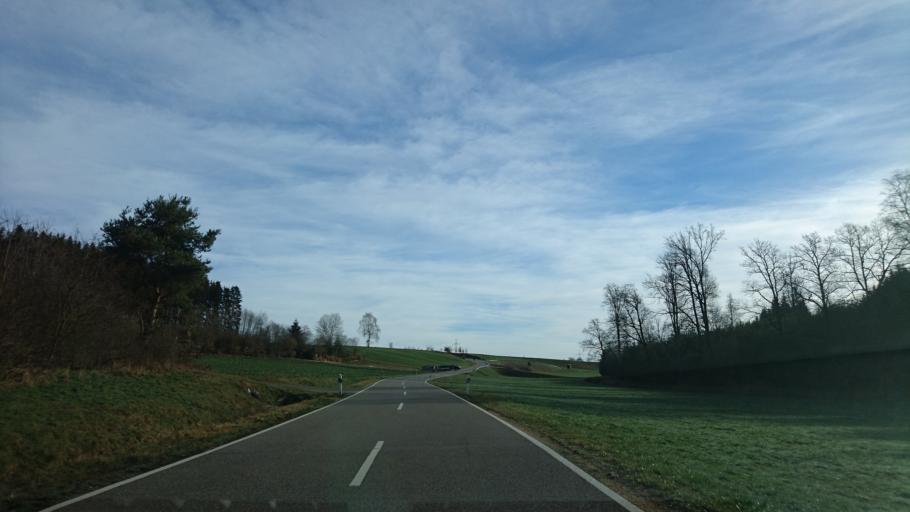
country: DE
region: Bavaria
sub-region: Swabia
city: Laugna
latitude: 48.5259
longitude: 10.7427
